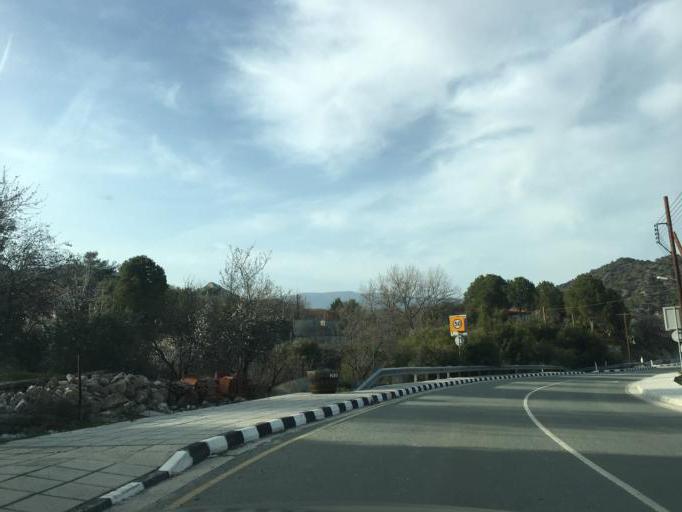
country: CY
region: Limassol
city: Pelendri
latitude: 34.8325
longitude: 32.9577
